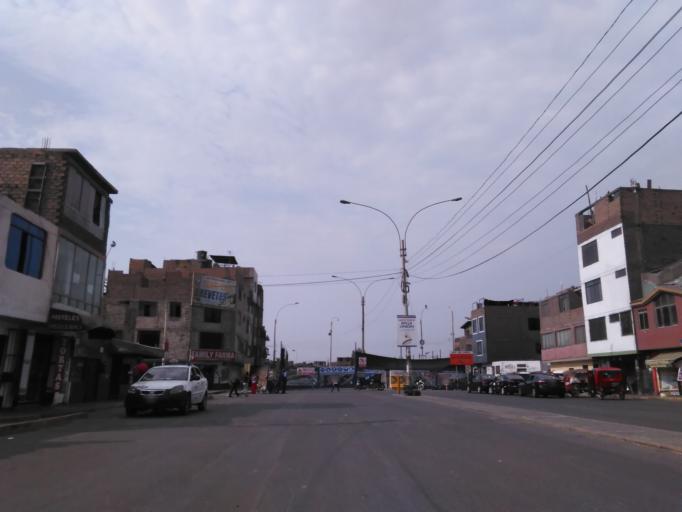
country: PE
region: Callao
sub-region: Callao
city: Callao
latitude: -12.0366
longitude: -77.0773
